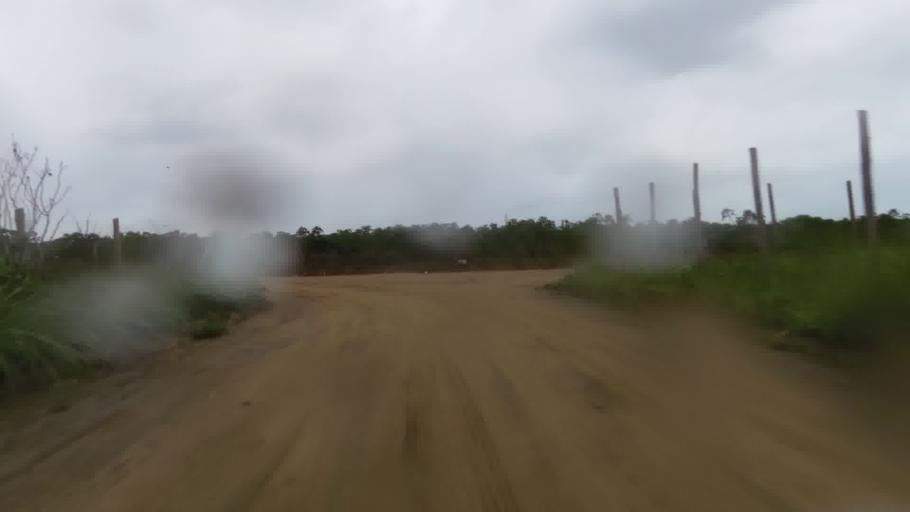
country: BR
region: Espirito Santo
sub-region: Marataizes
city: Marataizes
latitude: -21.0398
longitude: -40.8419
